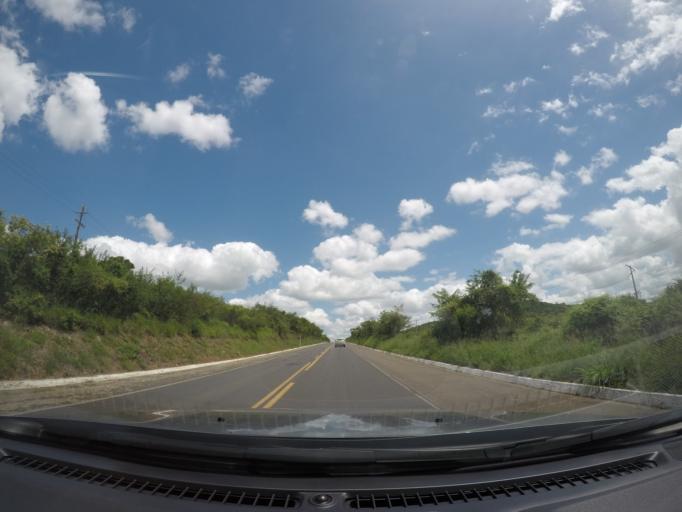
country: BR
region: Bahia
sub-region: Ipira
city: Ipira
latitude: -12.1734
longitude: -39.7233
